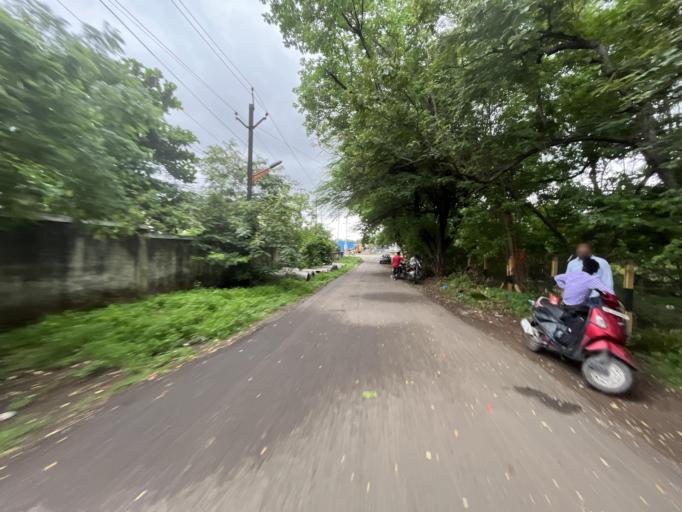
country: IN
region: Maharashtra
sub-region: Aurangabad Division
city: Aurangabad
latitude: 19.8827
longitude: 75.3716
